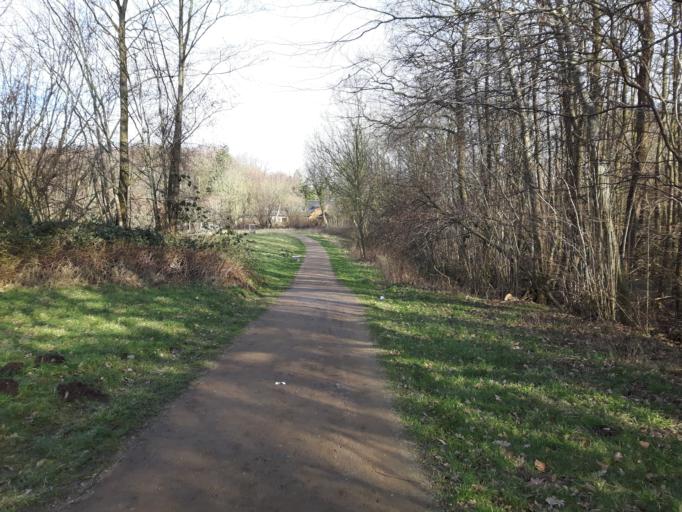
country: DE
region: Schleswig-Holstein
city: Muhbrook
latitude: 54.1400
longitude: 9.9923
